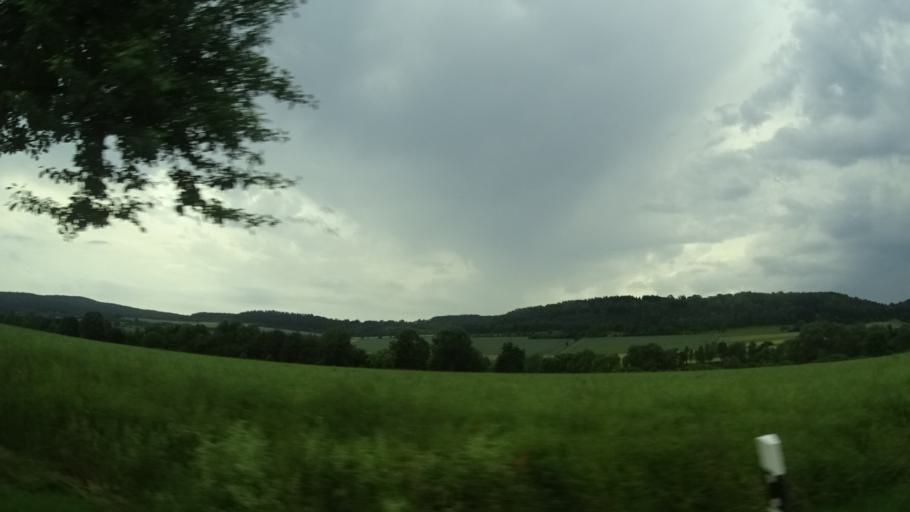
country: DE
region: Lower Saxony
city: Heinsen
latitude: 51.8920
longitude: 9.4219
